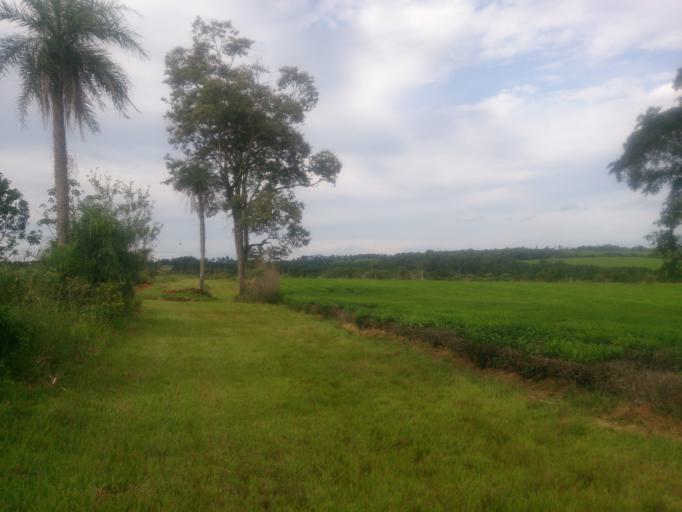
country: AR
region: Misiones
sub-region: Departamento de Obera
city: Obera
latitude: -27.4449
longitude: -55.1181
